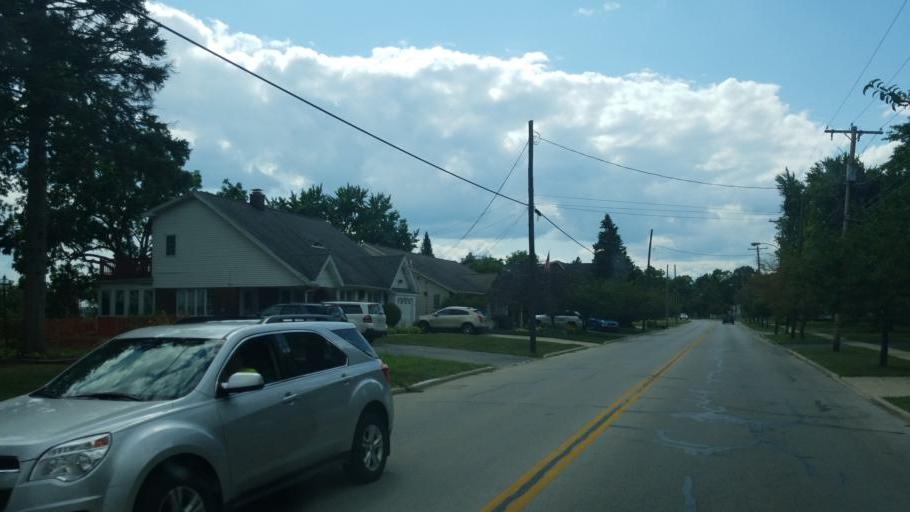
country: US
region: Ohio
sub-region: Wood County
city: Perrysburg
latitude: 41.5728
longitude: -83.6347
